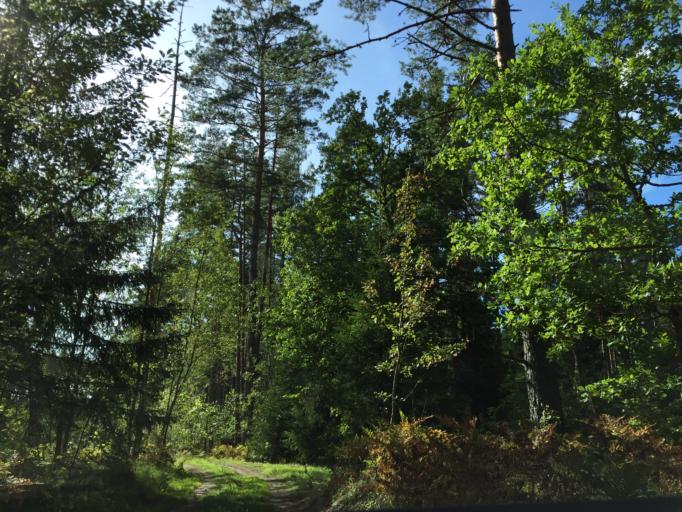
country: LV
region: Kuldigas Rajons
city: Kuldiga
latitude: 56.9937
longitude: 21.8150
